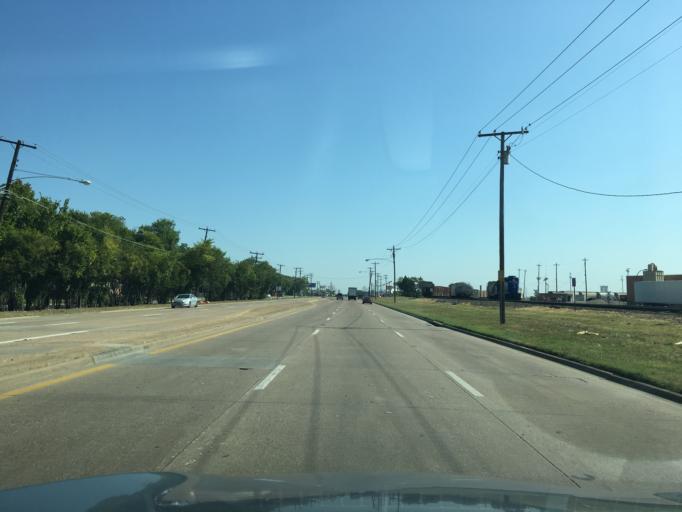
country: US
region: Texas
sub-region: Dallas County
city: Garland
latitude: 32.8557
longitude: -96.6767
